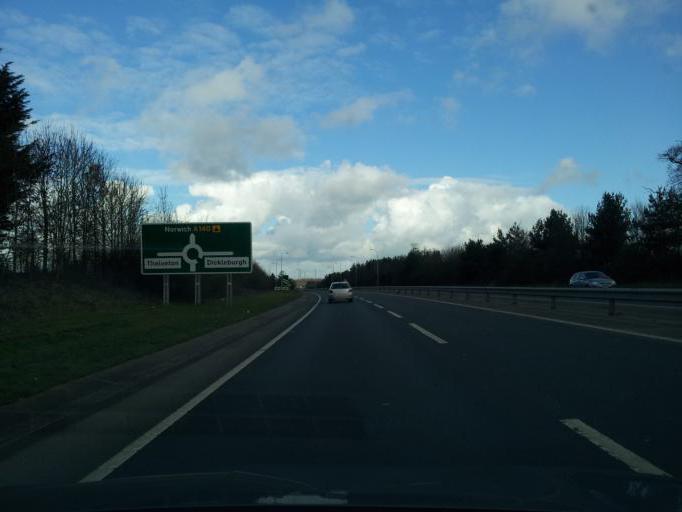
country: GB
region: England
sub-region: Norfolk
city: Diss
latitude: 52.3880
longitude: 1.1805
